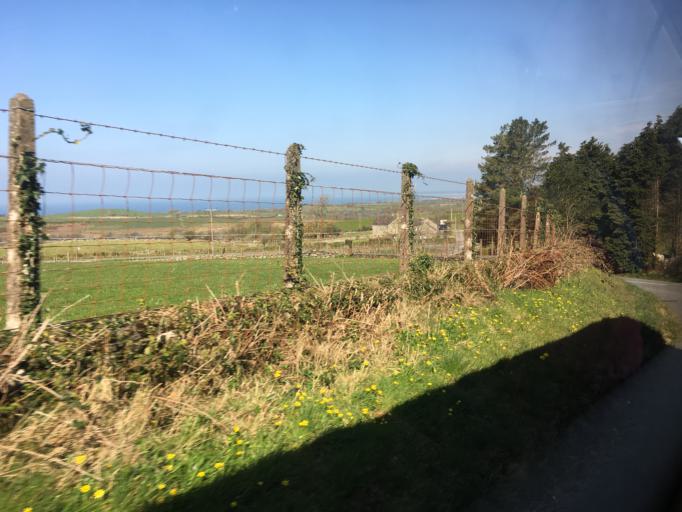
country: GB
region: Wales
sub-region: Gwynedd
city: Llanwnda
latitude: 53.0334
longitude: -4.2860
